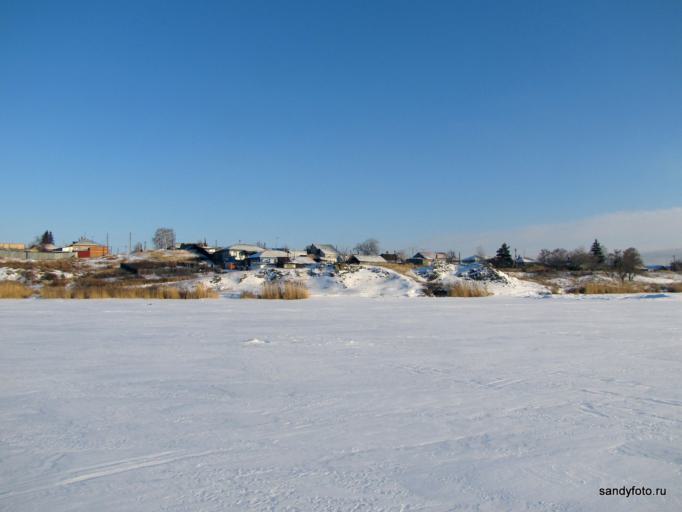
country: RU
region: Chelyabinsk
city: Troitsk
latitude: 54.0746
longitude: 61.5774
